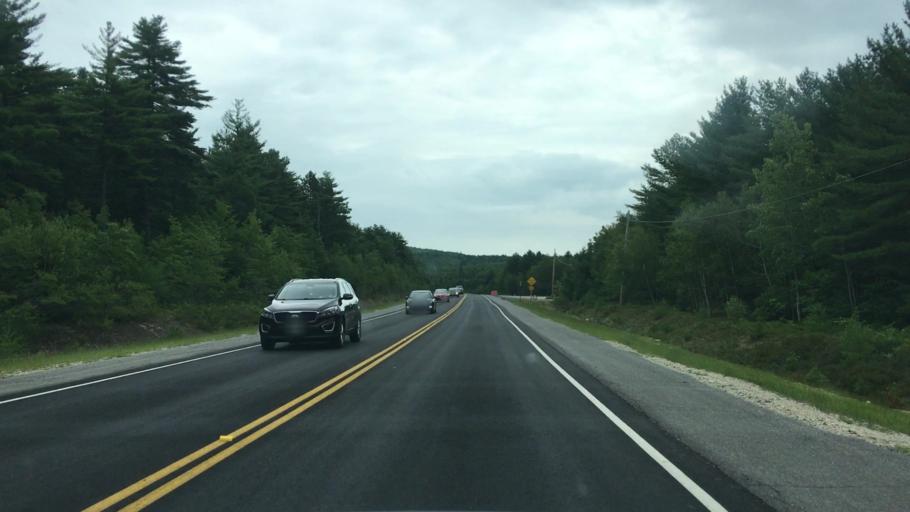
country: US
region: Maine
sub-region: Washington County
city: Cherryfield
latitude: 44.8785
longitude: -67.8720
